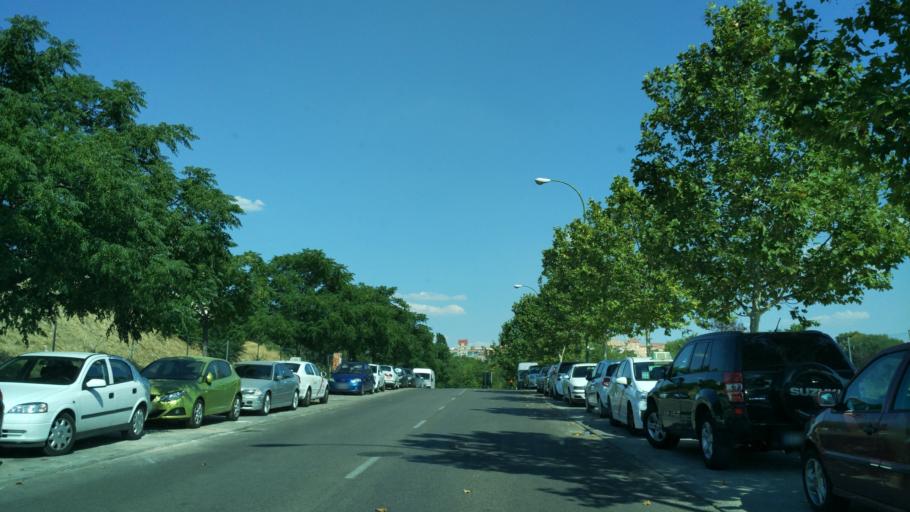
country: ES
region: Madrid
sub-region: Provincia de Madrid
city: Tetuan de las Victorias
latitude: 40.4716
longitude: -3.7160
